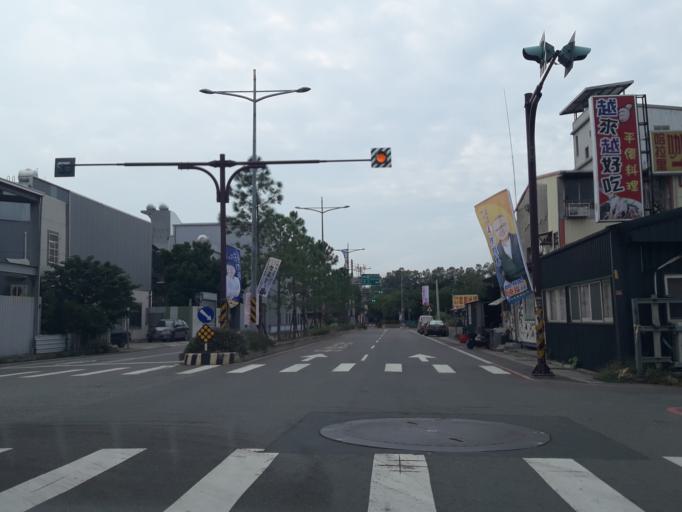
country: TW
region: Taiwan
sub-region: Hsinchu
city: Hsinchu
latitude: 24.6890
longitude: 120.8945
